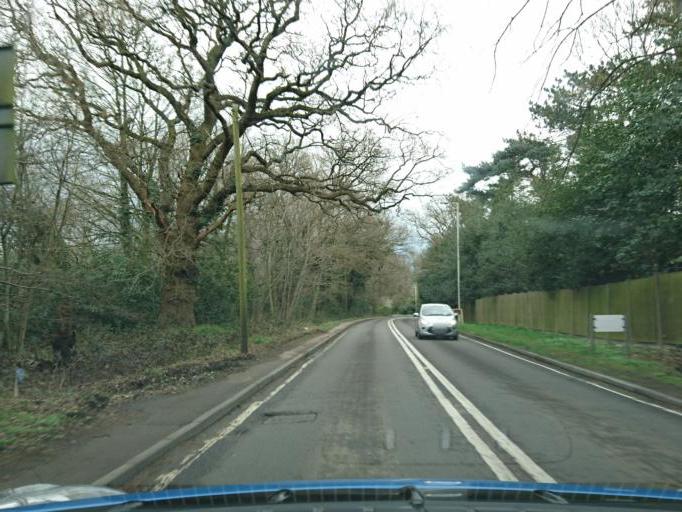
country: GB
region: England
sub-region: Hertfordshire
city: Borehamwood
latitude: 51.6448
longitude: -0.2716
